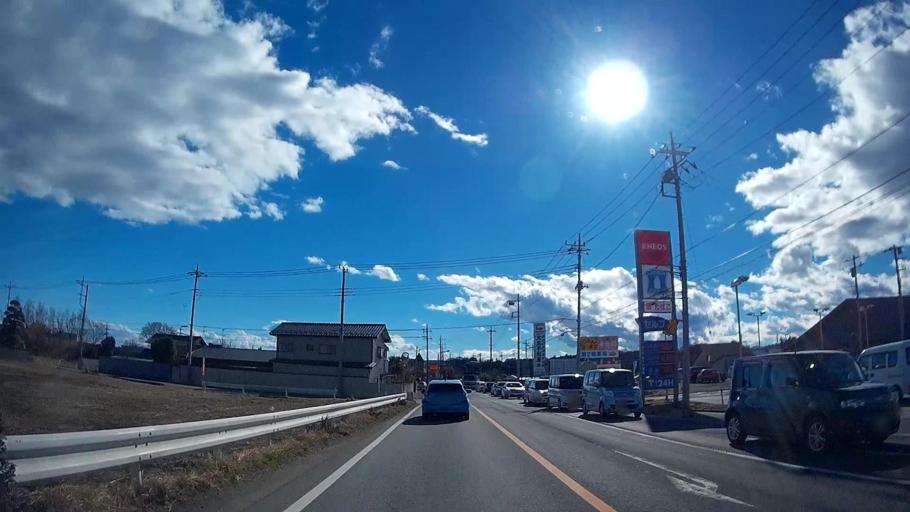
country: JP
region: Saitama
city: Yorii
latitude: 36.1217
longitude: 139.2408
